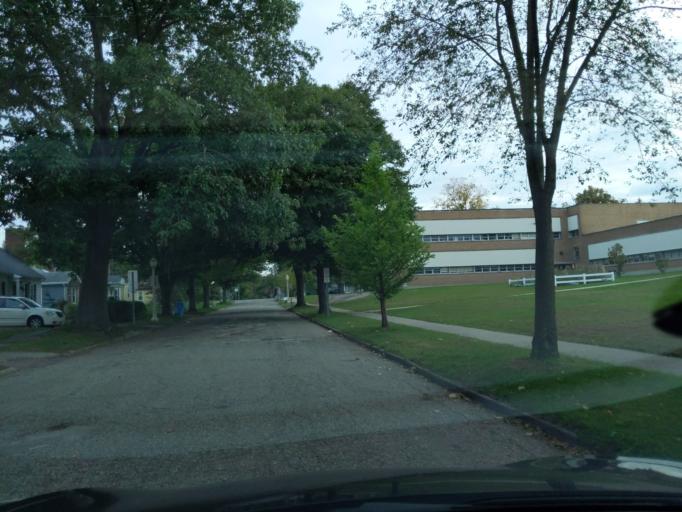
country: US
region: Michigan
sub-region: Ingham County
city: Lansing
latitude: 42.7130
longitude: -84.5339
